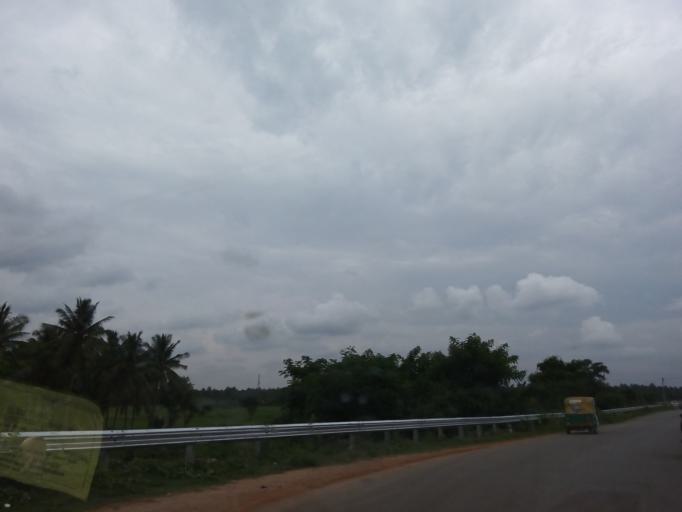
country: IN
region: Karnataka
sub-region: Hassan
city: Channarayapatna
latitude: 12.8780
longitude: 76.4243
